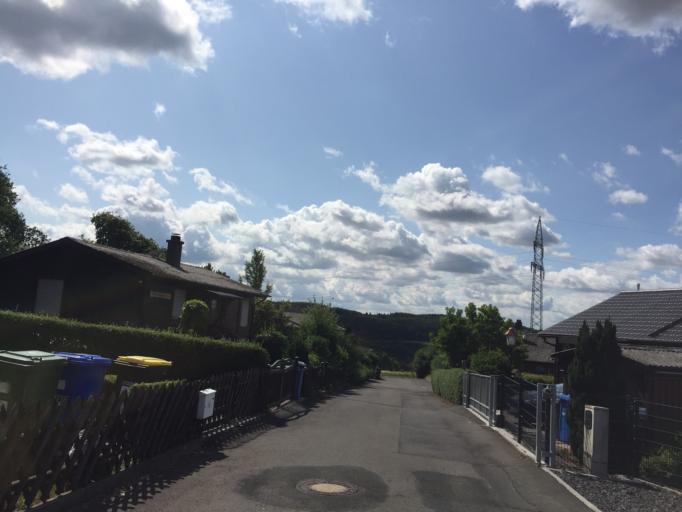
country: DE
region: Hesse
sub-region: Regierungsbezirk Giessen
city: Grunberg
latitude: 50.5791
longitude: 8.9747
